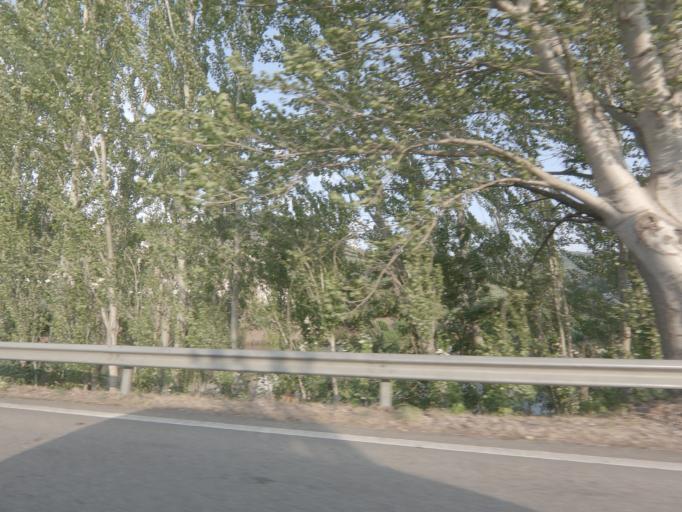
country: PT
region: Viseu
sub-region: Armamar
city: Armamar
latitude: 41.1504
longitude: -7.6836
